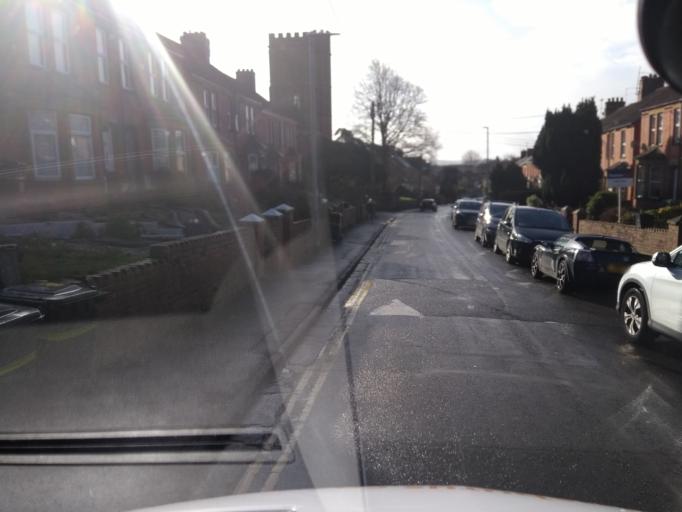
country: GB
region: England
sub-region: Somerset
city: Yeovil
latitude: 50.9480
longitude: -2.6209
